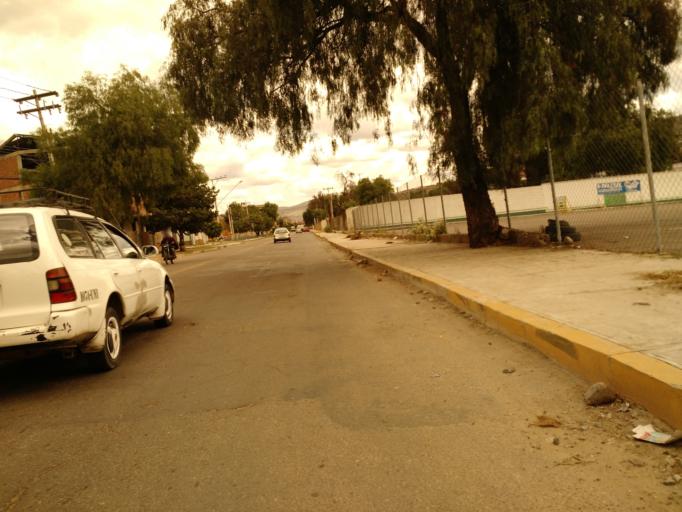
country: BO
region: Cochabamba
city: Cochabamba
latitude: -17.4174
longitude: -66.1279
